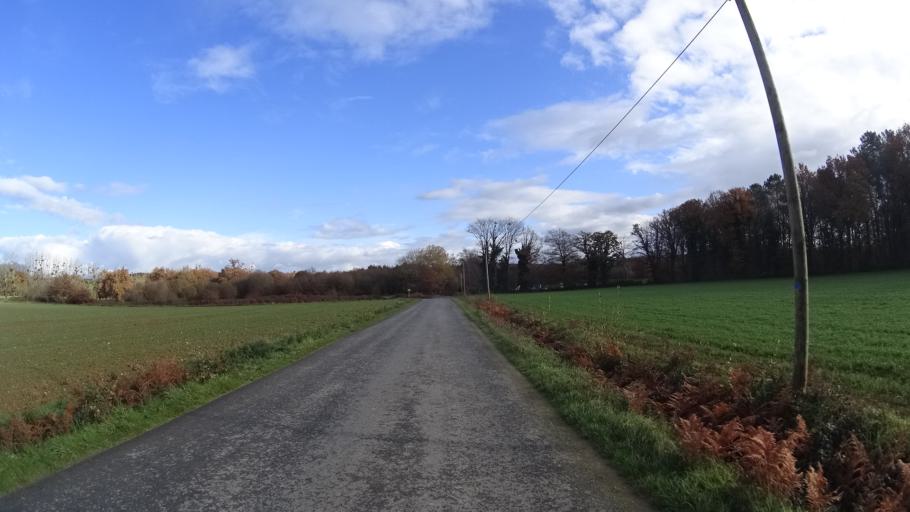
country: FR
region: Brittany
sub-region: Departement du Morbihan
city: Carentoir
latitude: 47.8221
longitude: -2.1174
